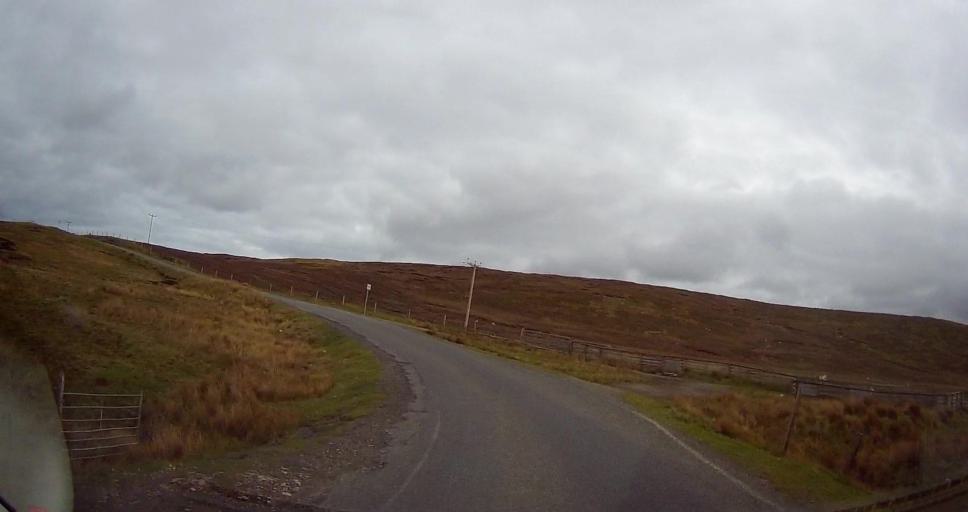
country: GB
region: Scotland
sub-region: Shetland Islands
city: Shetland
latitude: 60.6047
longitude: -1.0913
